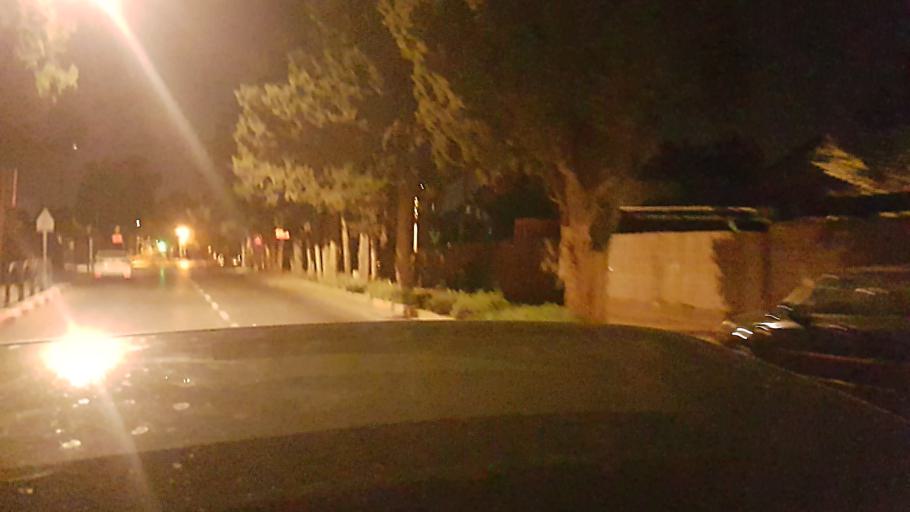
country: IL
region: Central District
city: Hod HaSharon
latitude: 32.1613
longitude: 34.8868
